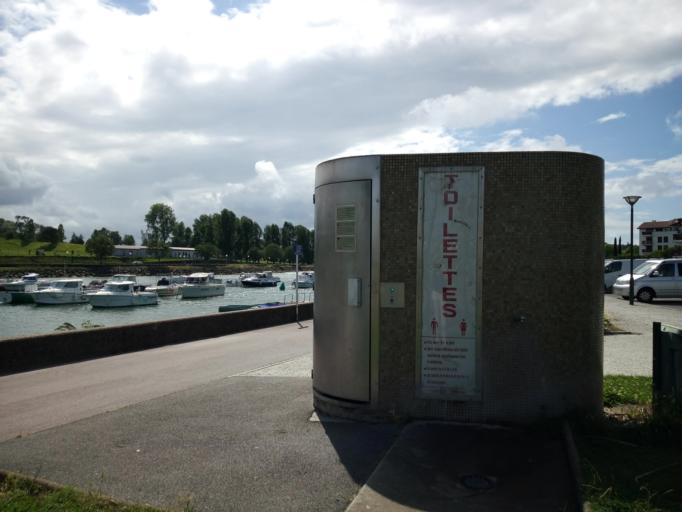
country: FR
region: Aquitaine
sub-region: Departement des Pyrenees-Atlantiques
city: Saint-Jean-de-Luz
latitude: 43.3814
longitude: -1.6542
